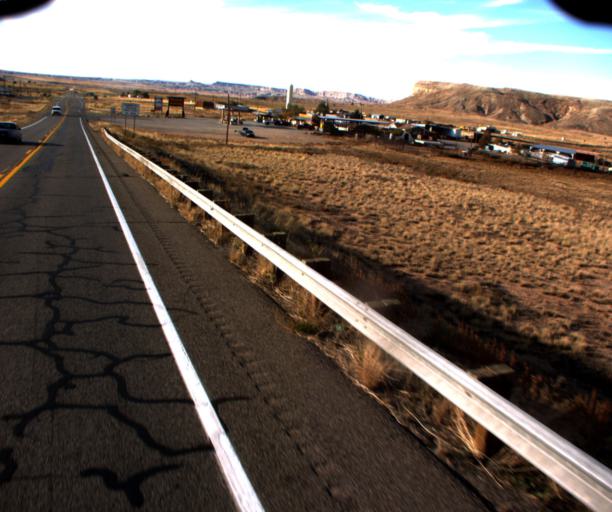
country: US
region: New Mexico
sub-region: San Juan County
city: Shiprock
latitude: 36.9184
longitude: -109.0828
